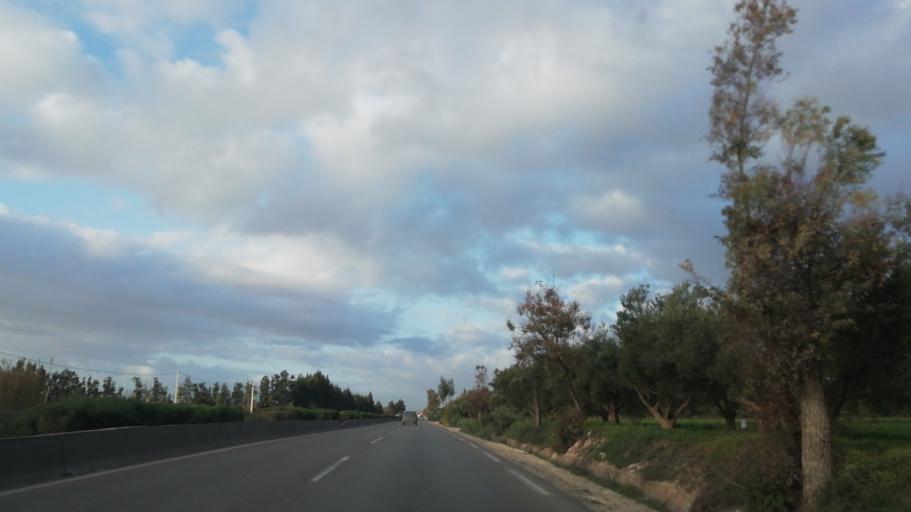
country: DZ
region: Oran
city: Mers el Kebir
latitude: 35.6050
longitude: -0.7583
